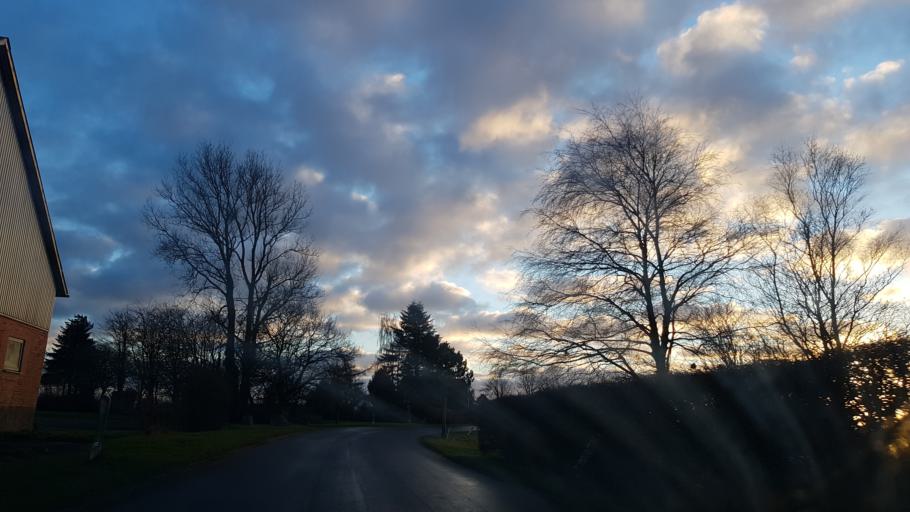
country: DK
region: South Denmark
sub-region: Kolding Kommune
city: Vamdrup
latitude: 55.3648
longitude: 9.3417
